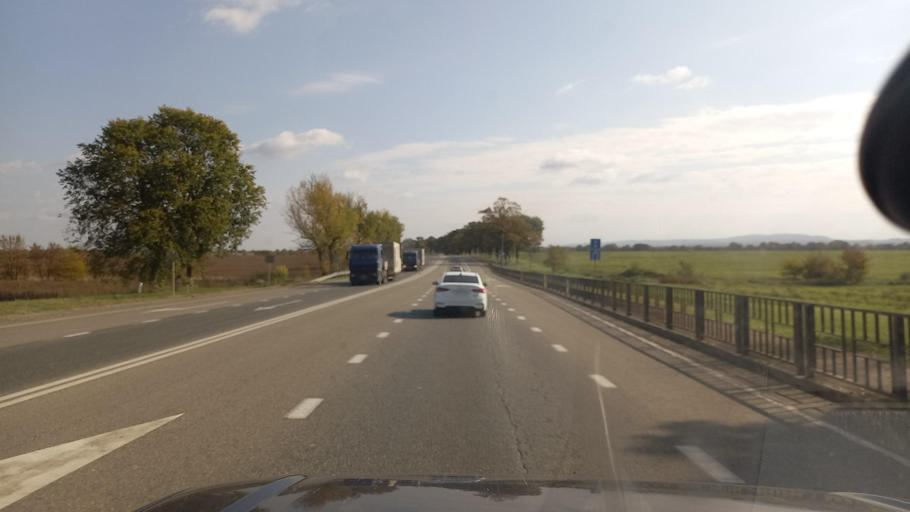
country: RU
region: Krasnodarskiy
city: Akhtyrskiy
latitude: 44.8546
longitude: 38.3348
